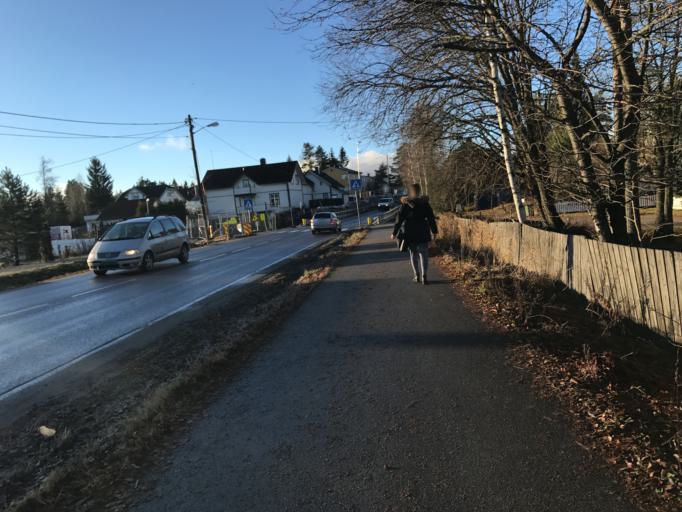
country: NO
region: Akershus
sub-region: Ullensaker
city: Jessheim
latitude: 60.1406
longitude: 11.1864
